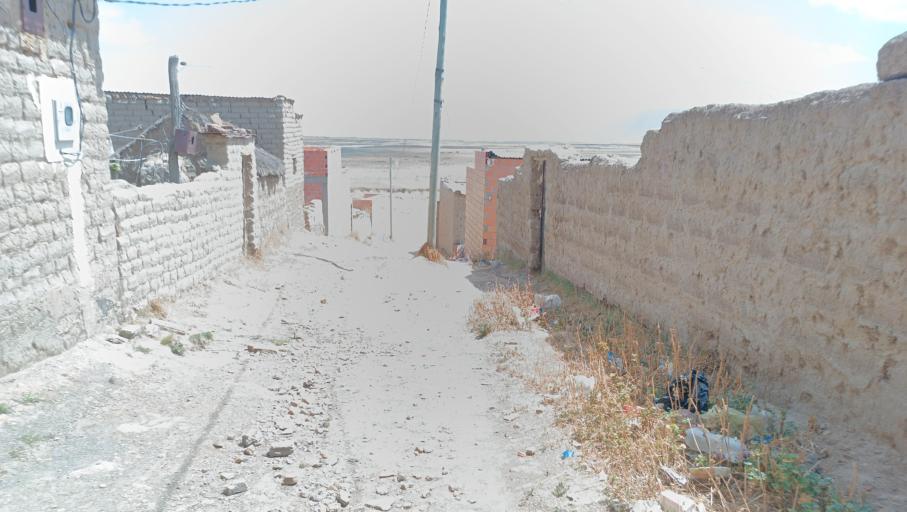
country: BO
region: La Paz
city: Batallas
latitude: -16.3854
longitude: -68.5966
